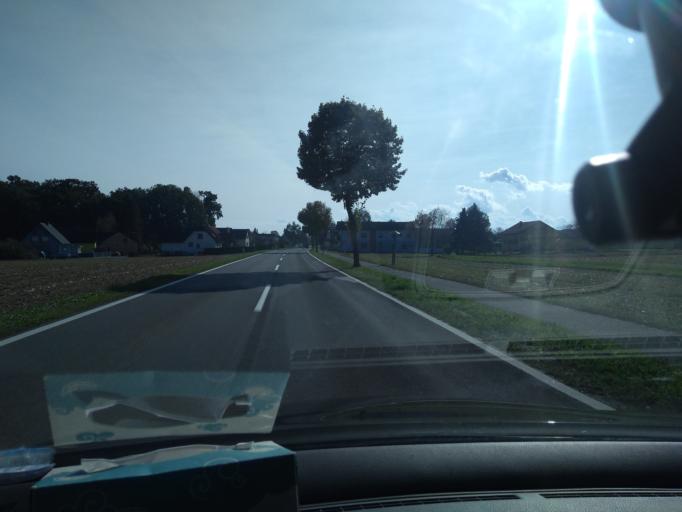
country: AT
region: Styria
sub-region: Politischer Bezirk Leibnitz
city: Kaindorf an der Sulm
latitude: 46.8306
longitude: 15.5434
